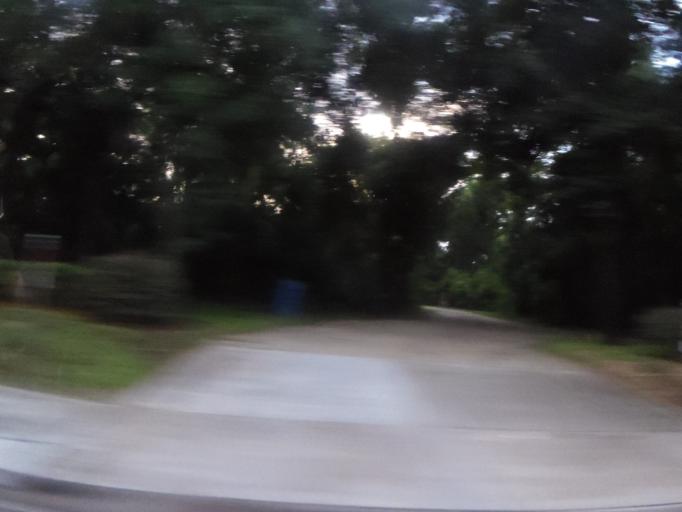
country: US
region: Florida
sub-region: Duval County
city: Jacksonville
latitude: 30.3669
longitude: -81.5617
